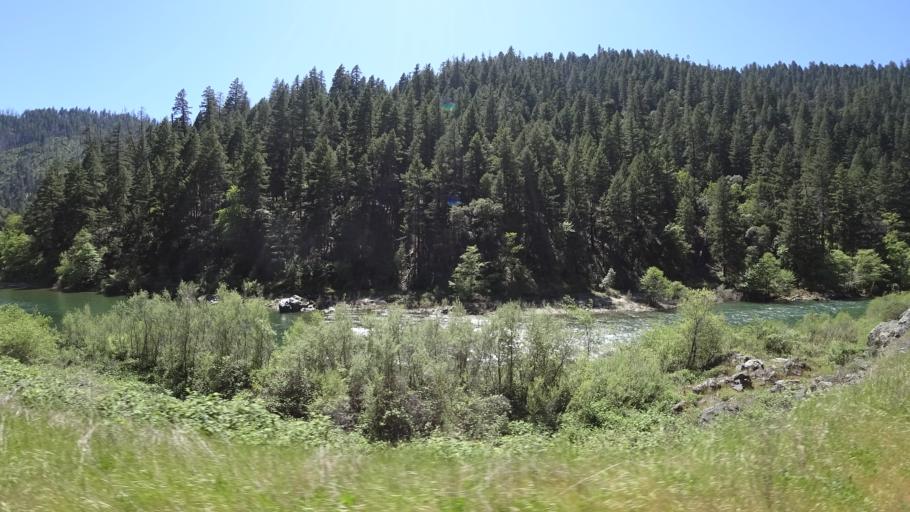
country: US
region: California
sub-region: Trinity County
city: Hayfork
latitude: 40.7718
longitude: -123.3091
